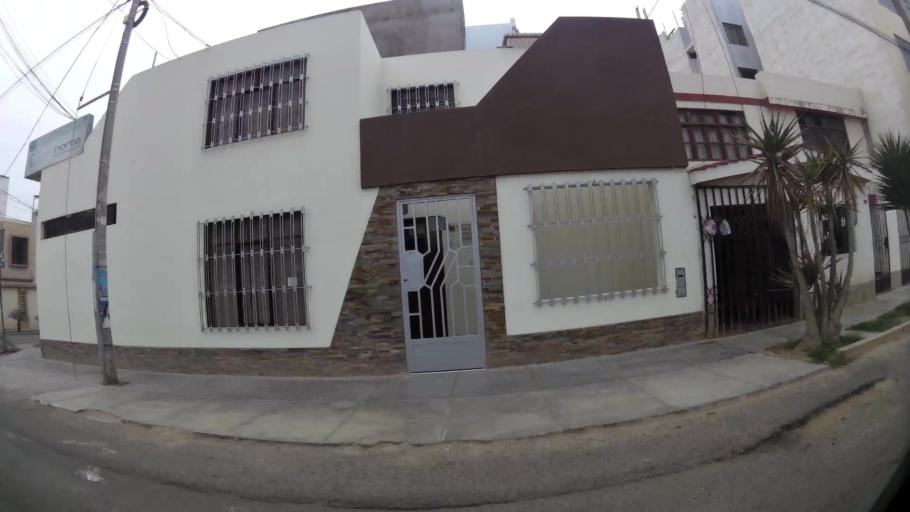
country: PE
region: La Libertad
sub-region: Provincia de Trujillo
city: Buenos Aires
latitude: -8.1314
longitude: -79.0430
